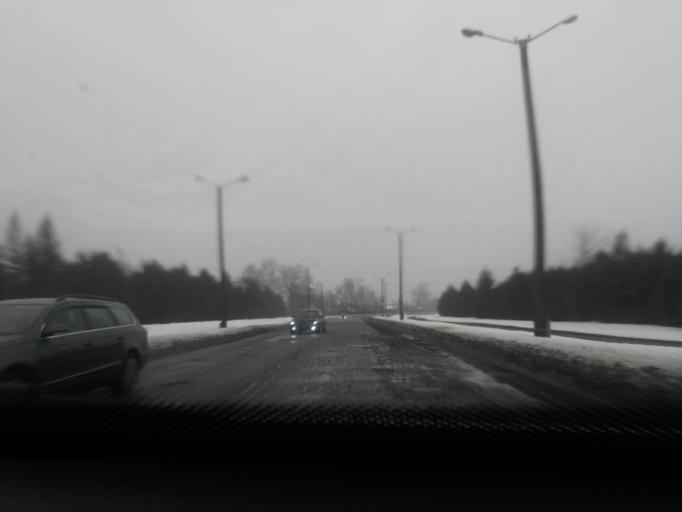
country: BY
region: Mogilev
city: Babruysk
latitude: 53.1888
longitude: 29.2174
